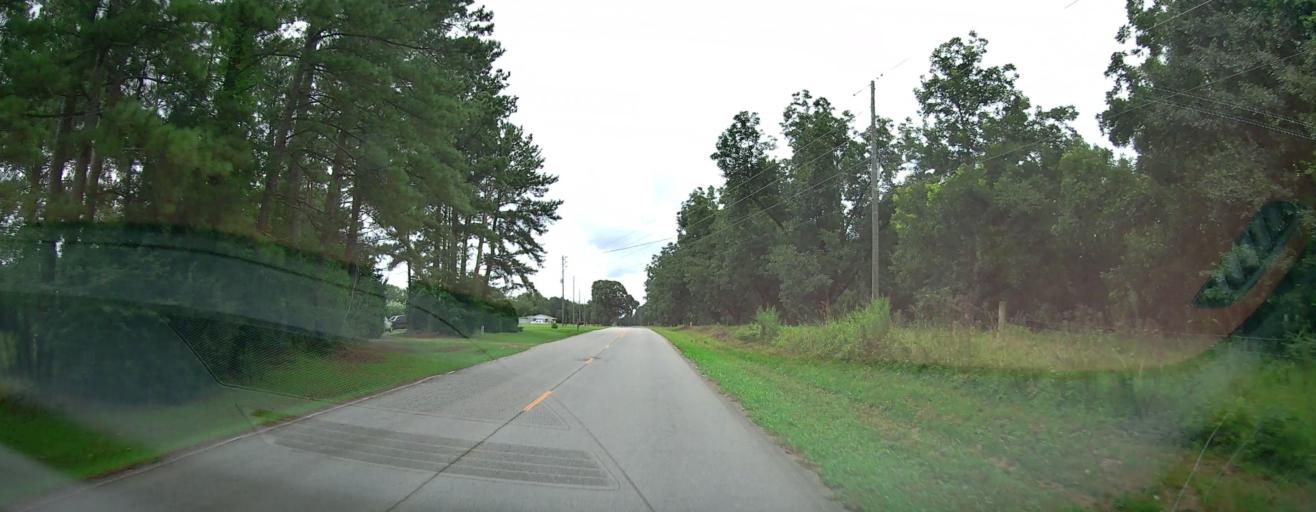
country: US
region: Georgia
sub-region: Peach County
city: Byron
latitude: 32.5740
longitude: -83.7510
